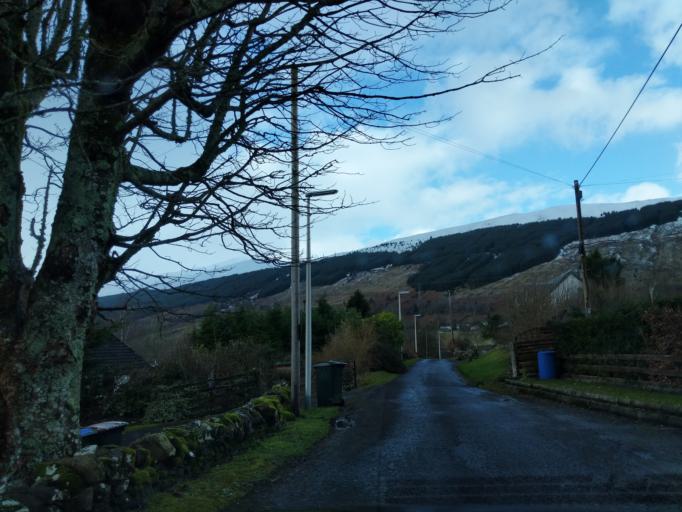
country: GB
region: Scotland
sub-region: Perth and Kinross
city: Comrie
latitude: 56.5760
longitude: -4.0784
